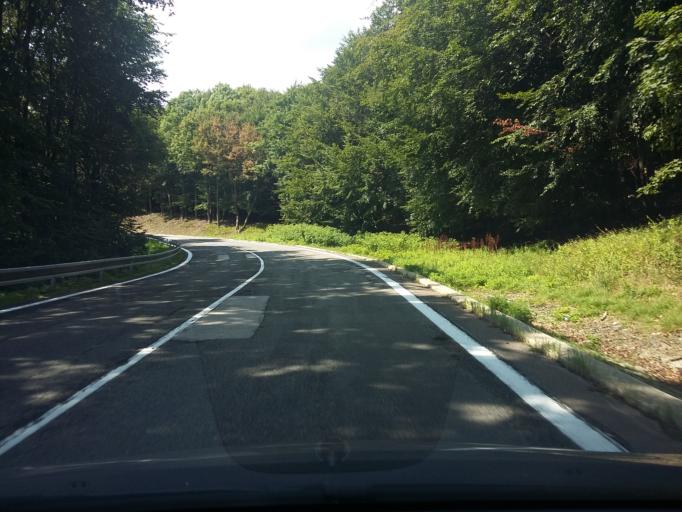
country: SK
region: Bratislavsky
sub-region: Okres Pezinok
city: Pezinok
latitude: 48.3530
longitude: 17.1930
